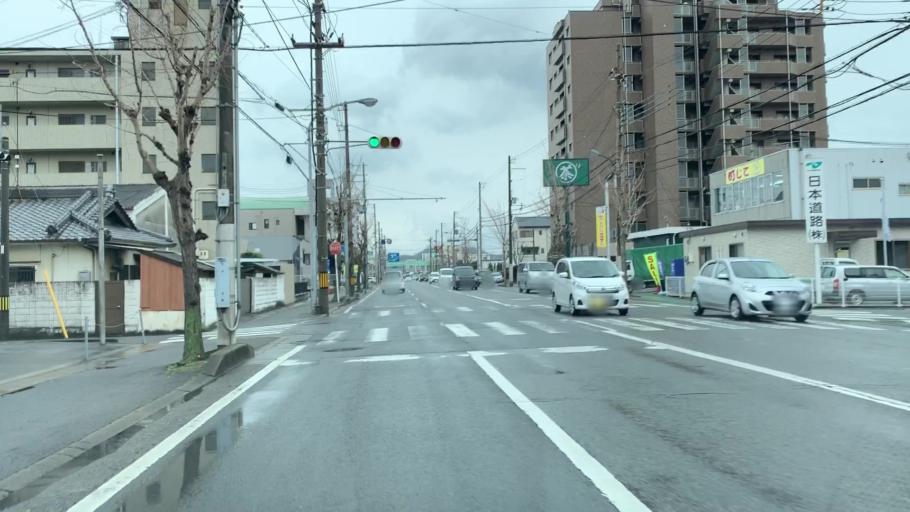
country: JP
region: Wakayama
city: Wakayama-shi
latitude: 34.2216
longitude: 135.1596
